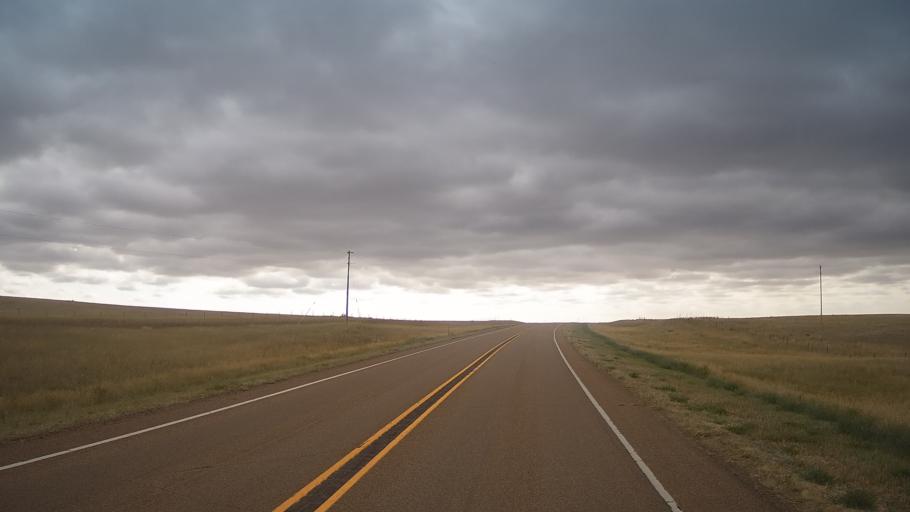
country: US
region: Montana
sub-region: Valley County
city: Glasgow
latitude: 48.3688
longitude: -106.7918
